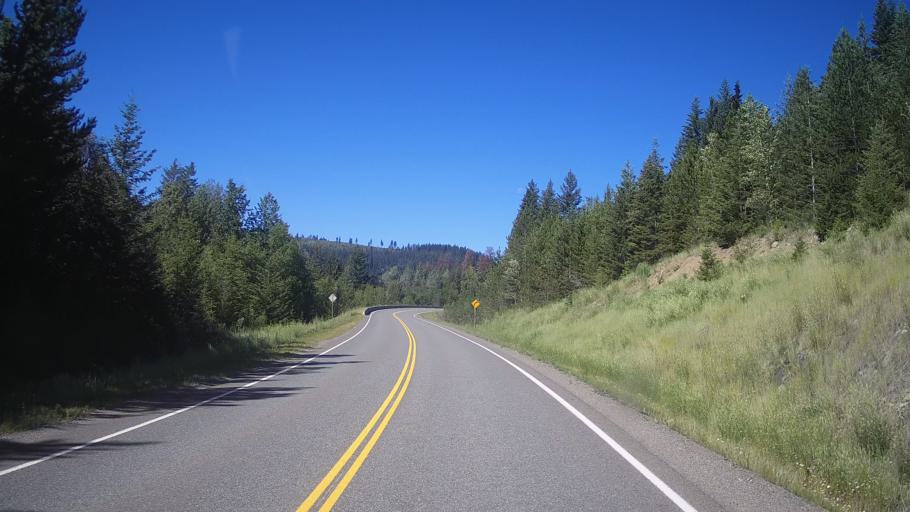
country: CA
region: British Columbia
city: Kamloops
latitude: 51.4734
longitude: -120.5462
